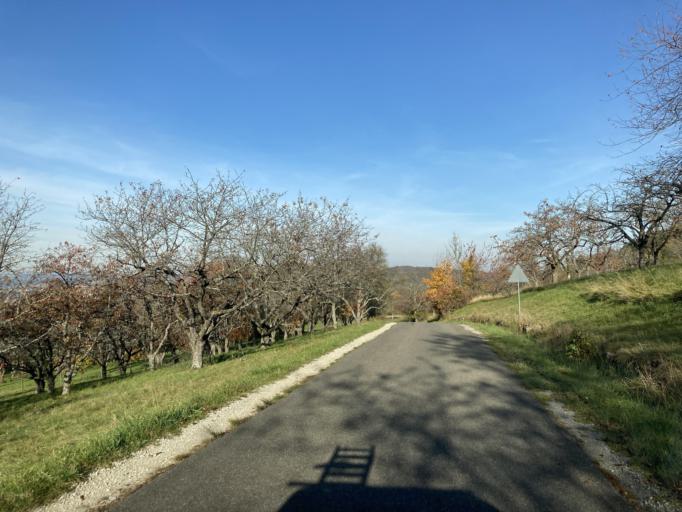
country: DE
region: Baden-Wuerttemberg
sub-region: Tuebingen Region
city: Mossingen
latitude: 48.3920
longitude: 9.0575
